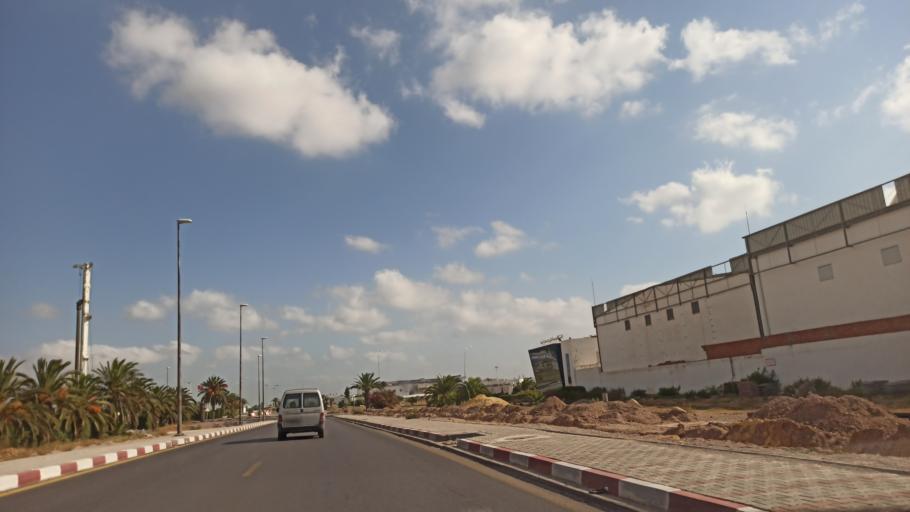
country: TN
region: Ariana
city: Ariana
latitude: 36.8418
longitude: 10.2151
